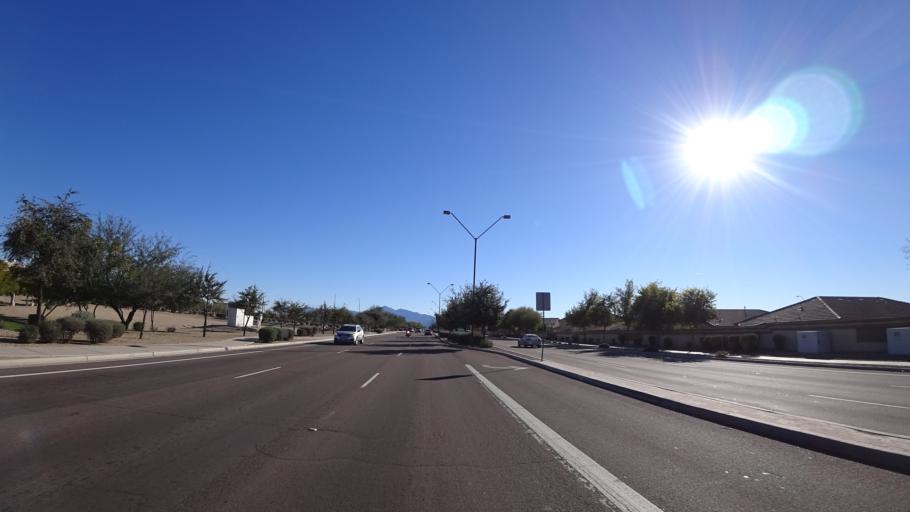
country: US
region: Arizona
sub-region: Maricopa County
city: Avondale
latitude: 33.4454
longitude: -112.3065
